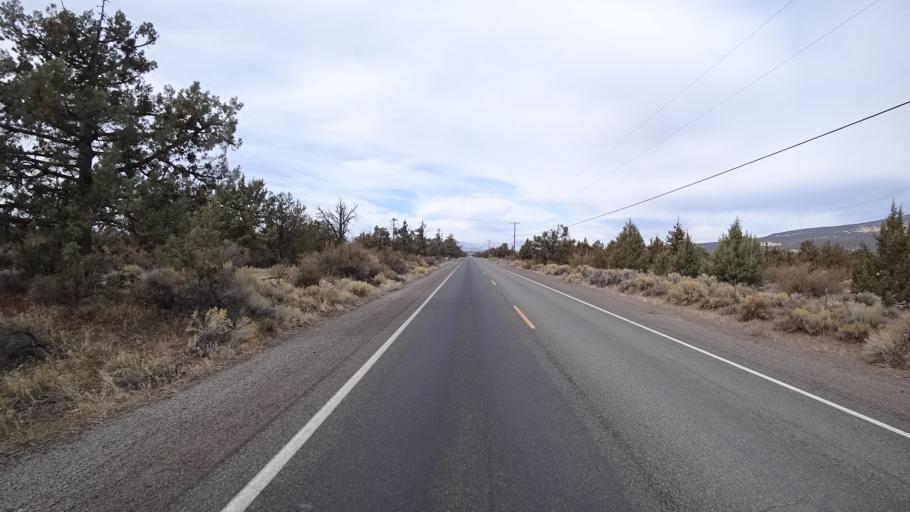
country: US
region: California
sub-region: Siskiyou County
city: Weed
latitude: 41.5811
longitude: -122.2901
